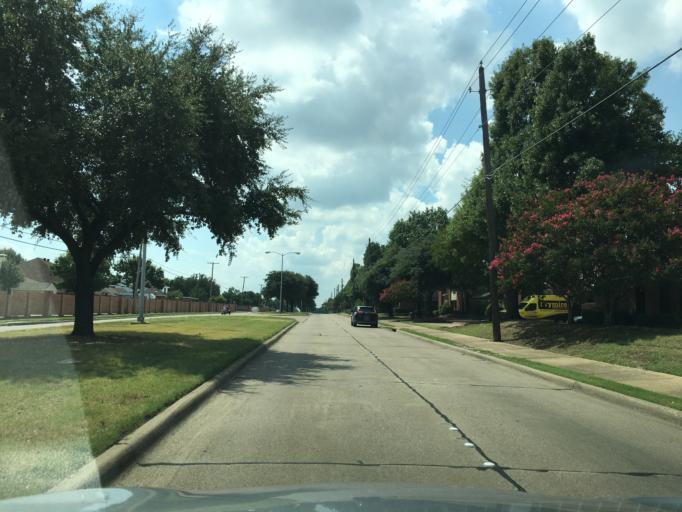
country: US
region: Texas
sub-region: Dallas County
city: Garland
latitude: 32.9434
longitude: -96.6482
